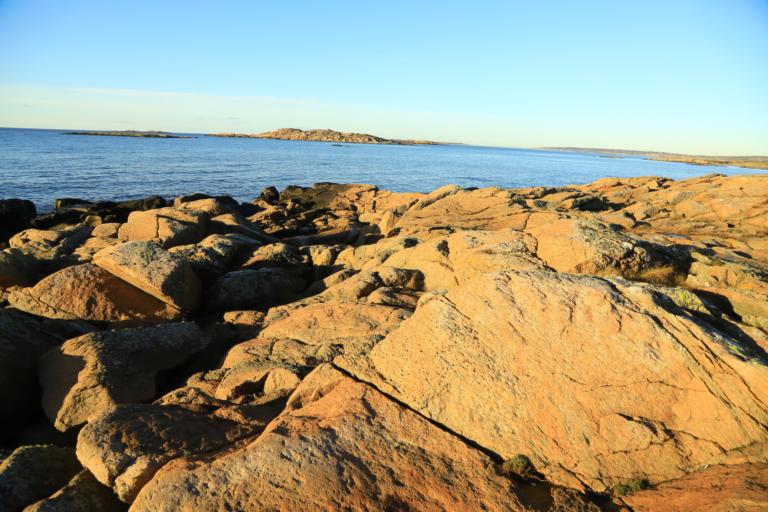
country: SE
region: Halland
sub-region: Varbergs Kommun
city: Varberg
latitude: 57.1881
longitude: 12.1539
